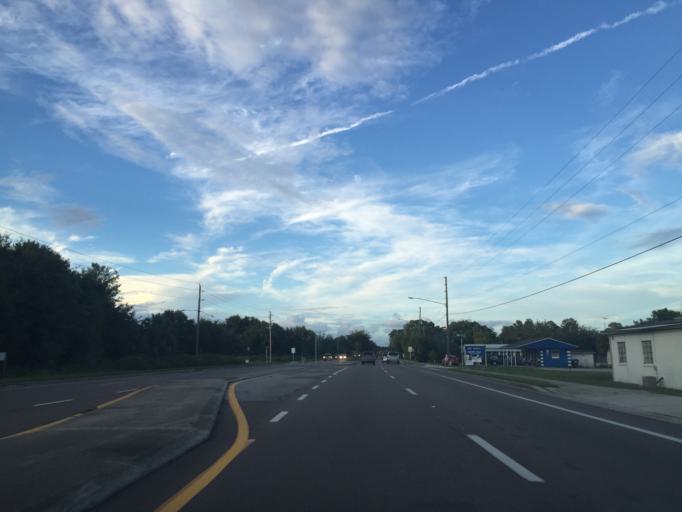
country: US
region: Florida
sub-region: Lake County
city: Tavares
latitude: 28.7913
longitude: -81.7455
